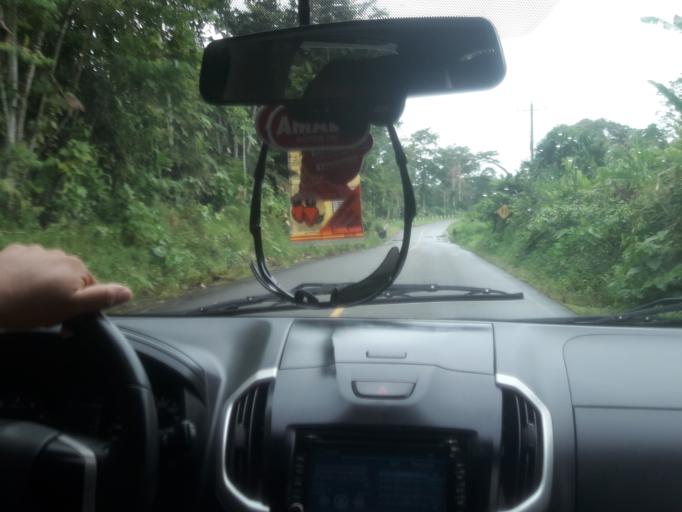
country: EC
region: Napo
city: Tena
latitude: -1.0343
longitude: -77.6878
